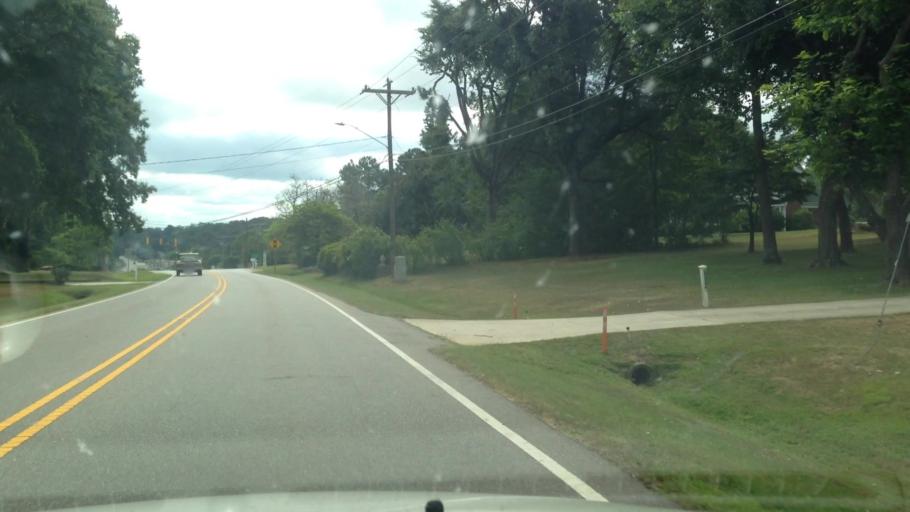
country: US
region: North Carolina
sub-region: Rockingham County
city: Madison
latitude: 36.3821
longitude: -79.9879
